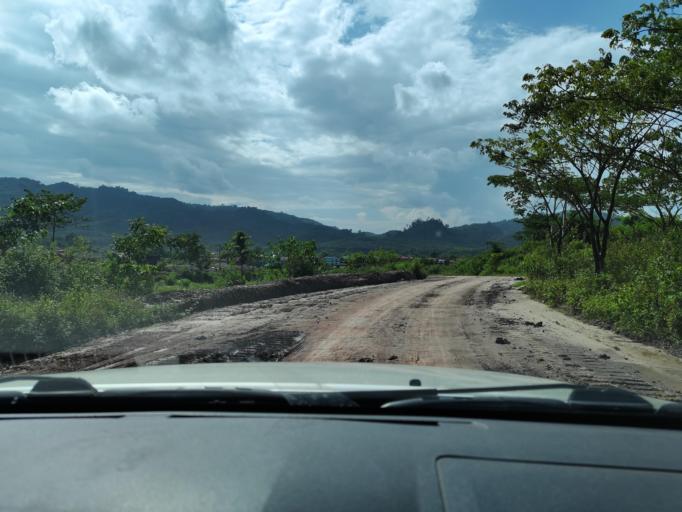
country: LA
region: Loungnamtha
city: Muang Nale
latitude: 20.5882
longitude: 101.0597
